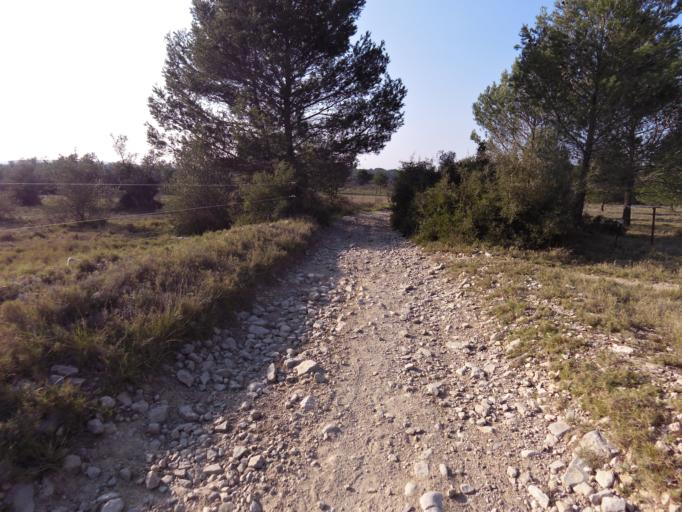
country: FR
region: Languedoc-Roussillon
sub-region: Departement du Gard
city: Gallargues-le-Montueux
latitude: 43.7300
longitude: 4.1642
